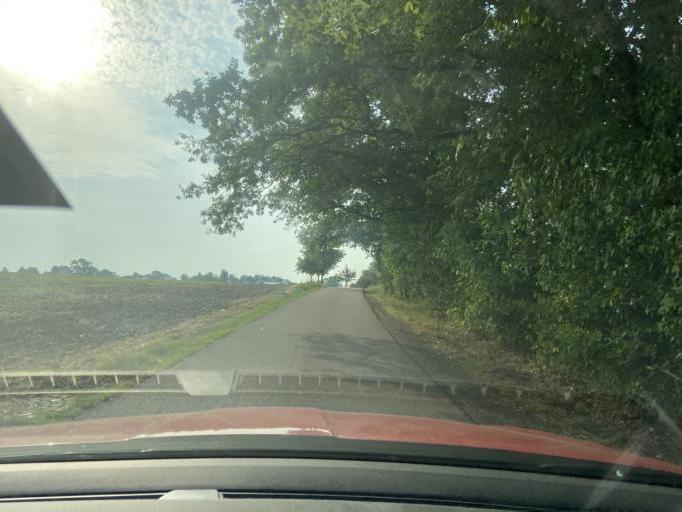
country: DE
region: Saxony
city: Tharandt
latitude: 51.0070
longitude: 13.5838
